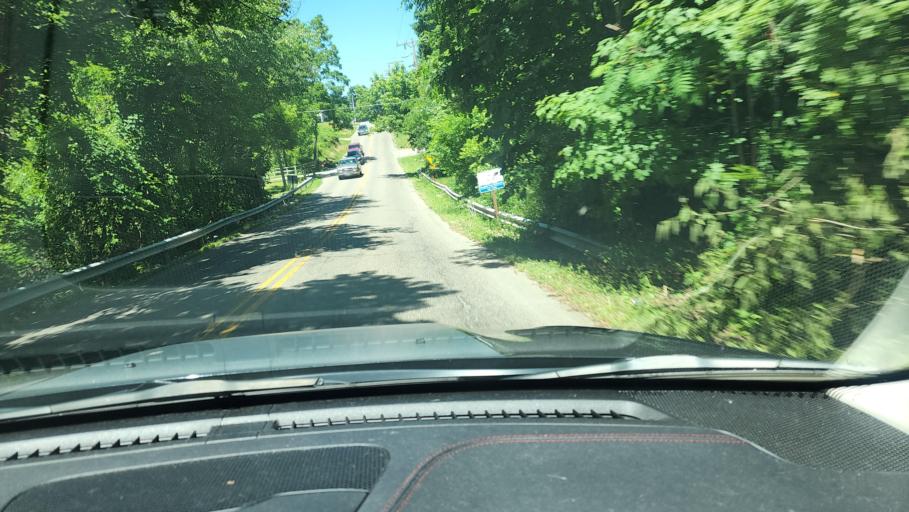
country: US
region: Ohio
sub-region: Mahoning County
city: Austintown
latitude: 41.0975
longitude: -80.7918
